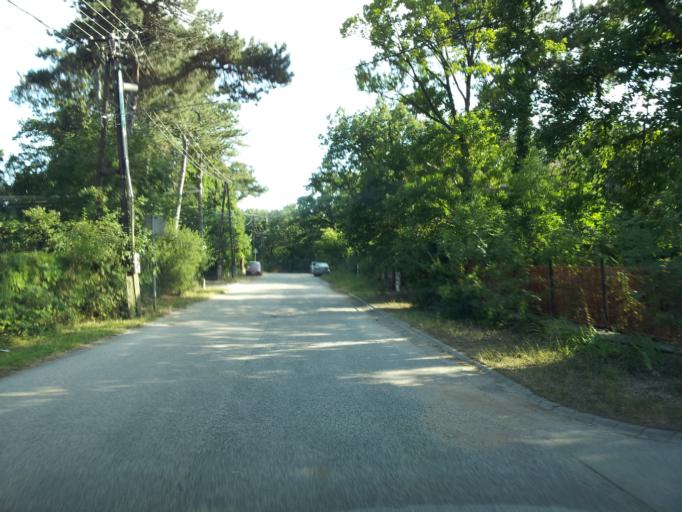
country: HU
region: Veszprem
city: Balatonalmadi
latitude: 47.0120
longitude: 17.9992
